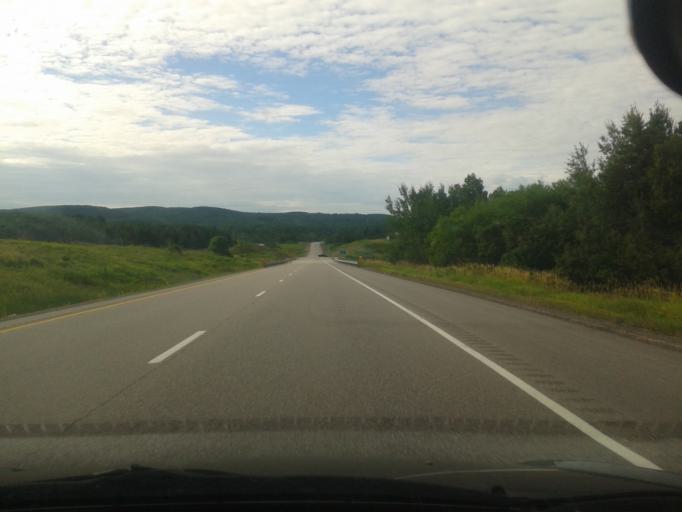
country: CA
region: Ontario
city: Powassan
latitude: 46.0535
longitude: -79.3470
